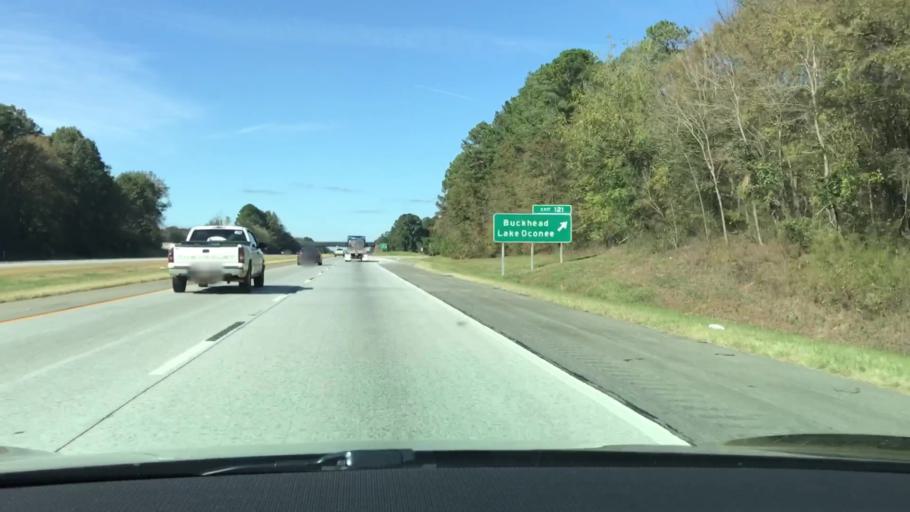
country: US
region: Georgia
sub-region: Putnam County
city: Jefferson
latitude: 33.5496
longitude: -83.3507
